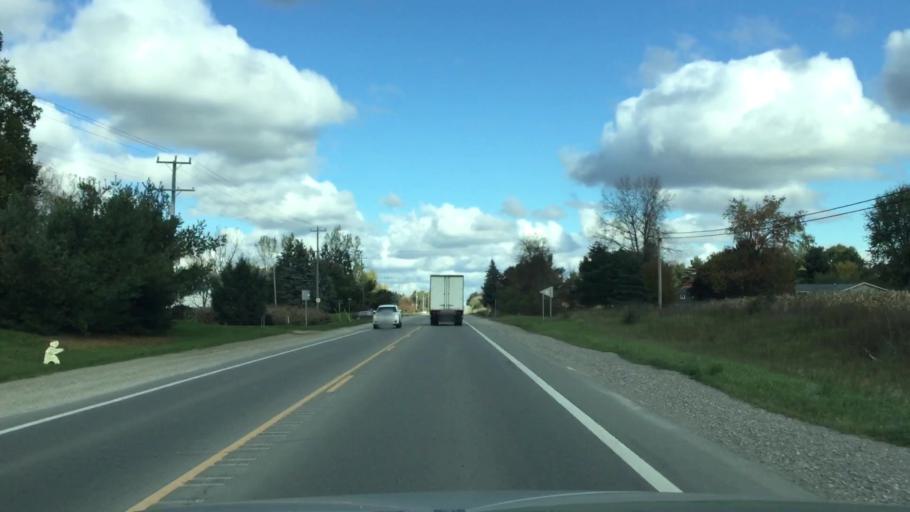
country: US
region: Michigan
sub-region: Oakland County
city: Oxford
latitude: 42.9164
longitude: -83.3126
